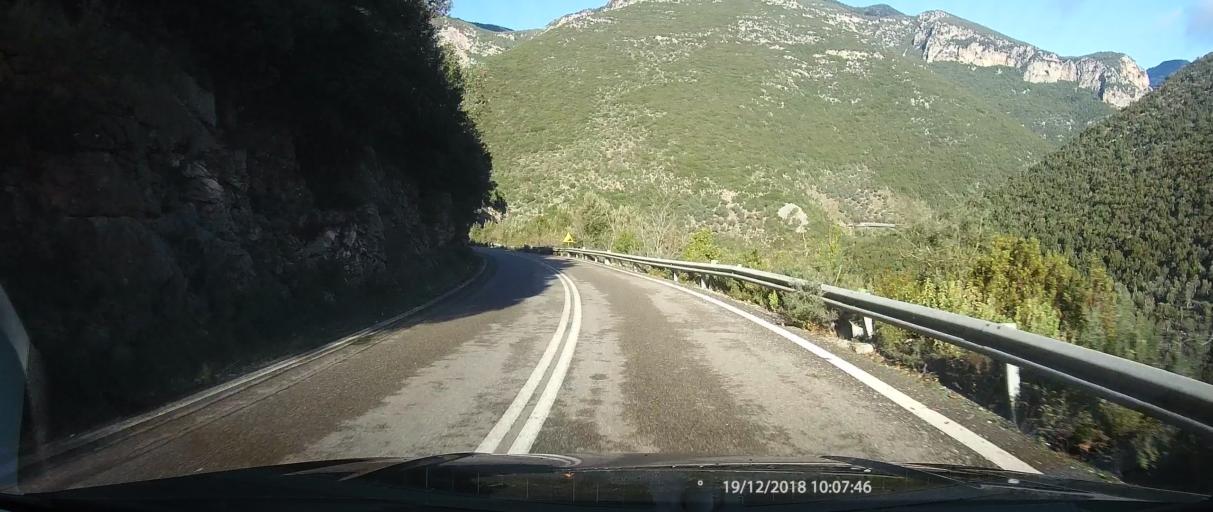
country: GR
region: Peloponnese
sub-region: Nomos Messinias
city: Paralia Vergas
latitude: 37.1145
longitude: 22.2098
